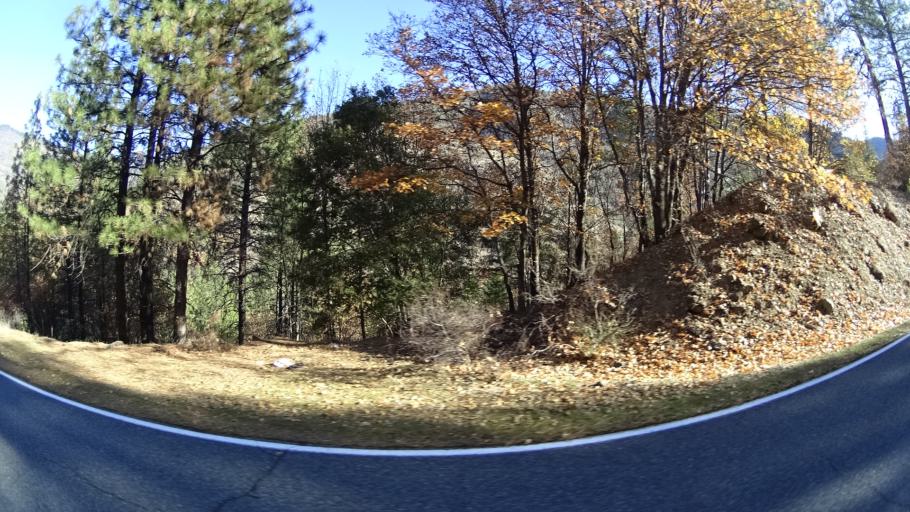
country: US
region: California
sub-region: Siskiyou County
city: Yreka
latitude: 41.9068
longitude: -122.8344
